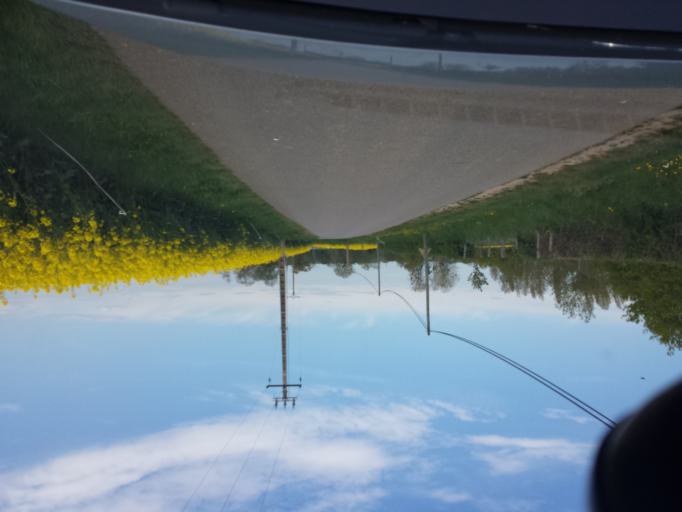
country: FR
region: Haute-Normandie
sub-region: Departement de l'Eure
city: Breteuil
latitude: 48.8024
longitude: 0.9369
